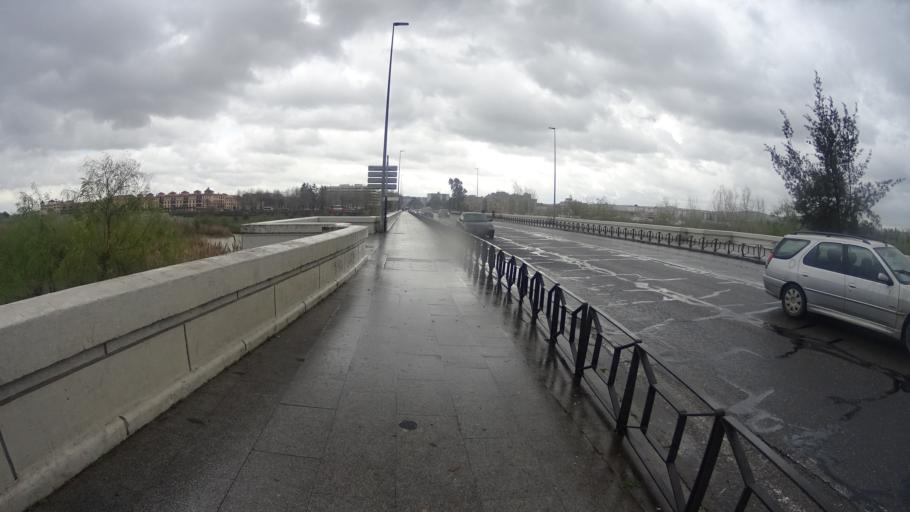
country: ES
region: Andalusia
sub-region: Province of Cordoba
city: Cordoba
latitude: 37.8726
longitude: -4.7836
